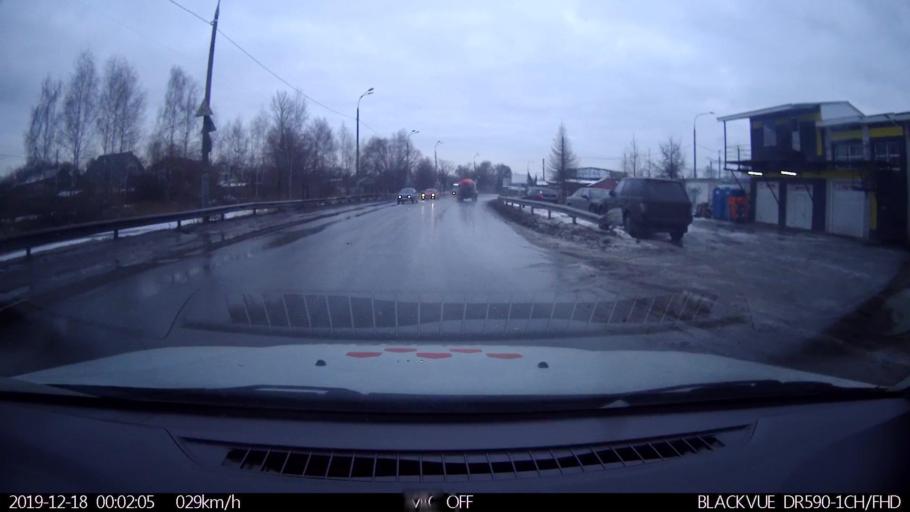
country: RU
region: Nizjnij Novgorod
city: Gorbatovka
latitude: 56.3706
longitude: 43.8255
